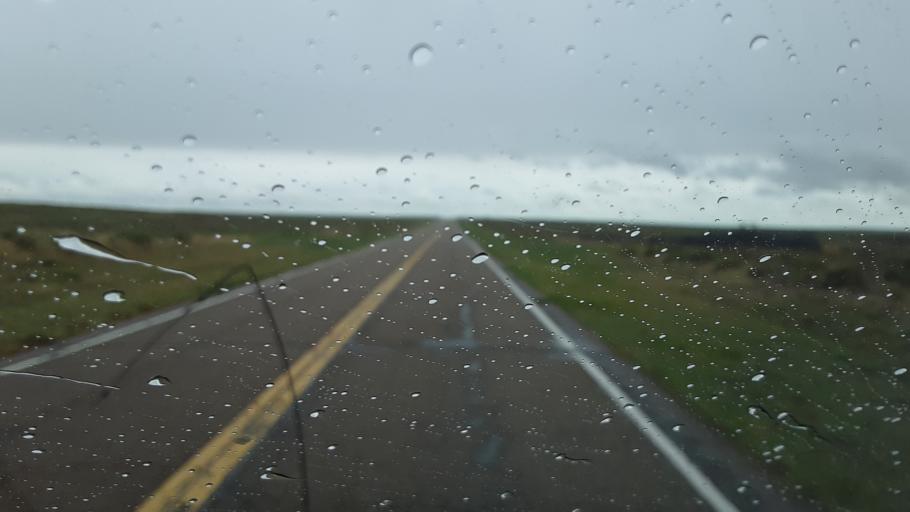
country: US
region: Colorado
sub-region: Lincoln County
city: Hugo
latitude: 38.8494
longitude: -103.2385
